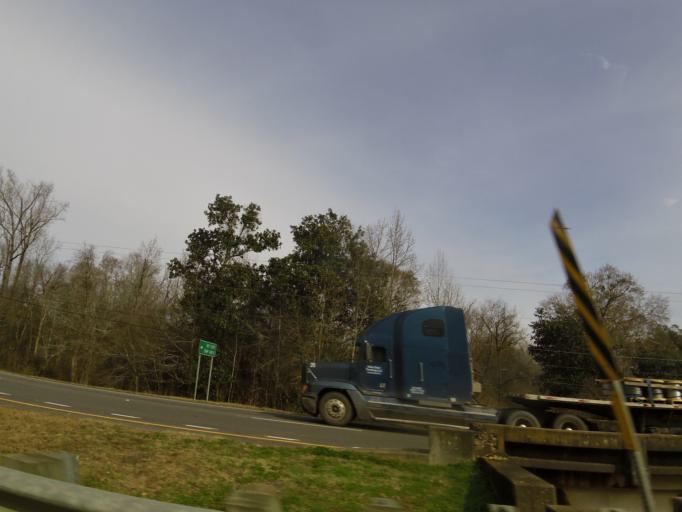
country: US
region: Alabama
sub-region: Dale County
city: Ozark
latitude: 31.4584
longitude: -85.6676
